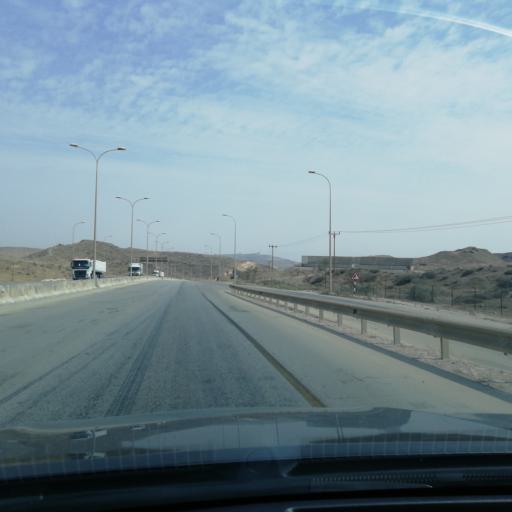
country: OM
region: Zufar
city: Salalah
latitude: 17.2593
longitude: 54.0833
